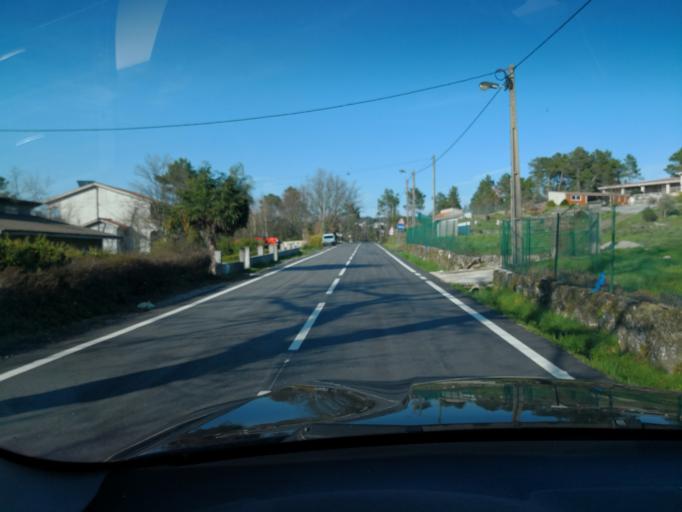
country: PT
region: Vila Real
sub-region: Vila Real
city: Vila Real
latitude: 41.3432
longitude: -7.6562
